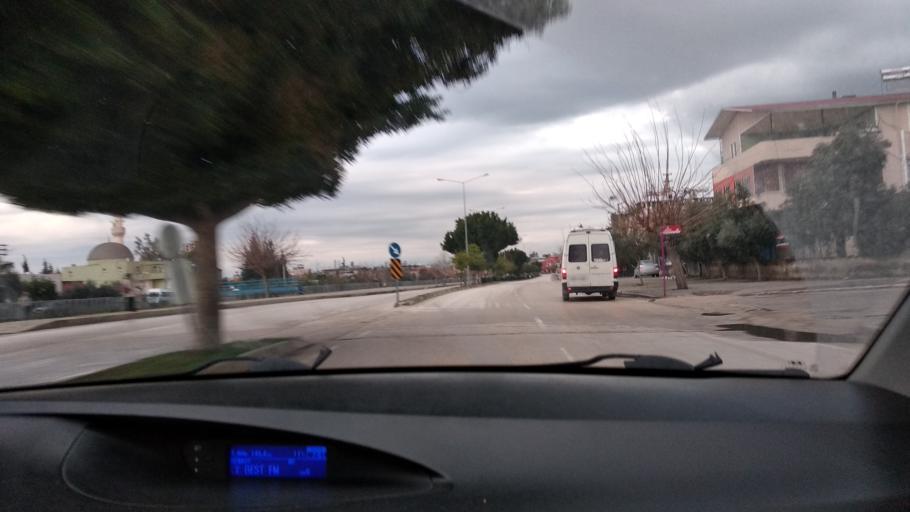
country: TR
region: Adana
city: Yuregir
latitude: 37.0115
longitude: 35.3884
